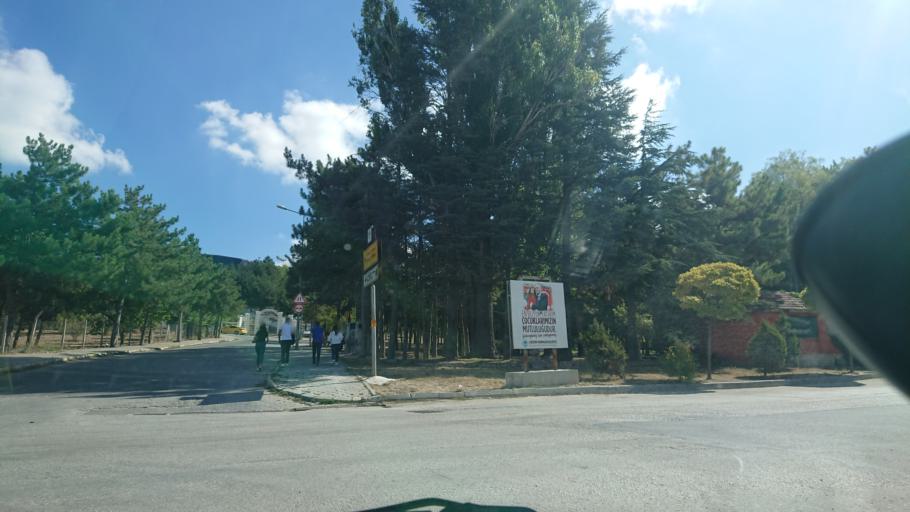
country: TR
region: Eskisehir
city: Eskisehir
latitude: 39.7587
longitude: 30.5300
